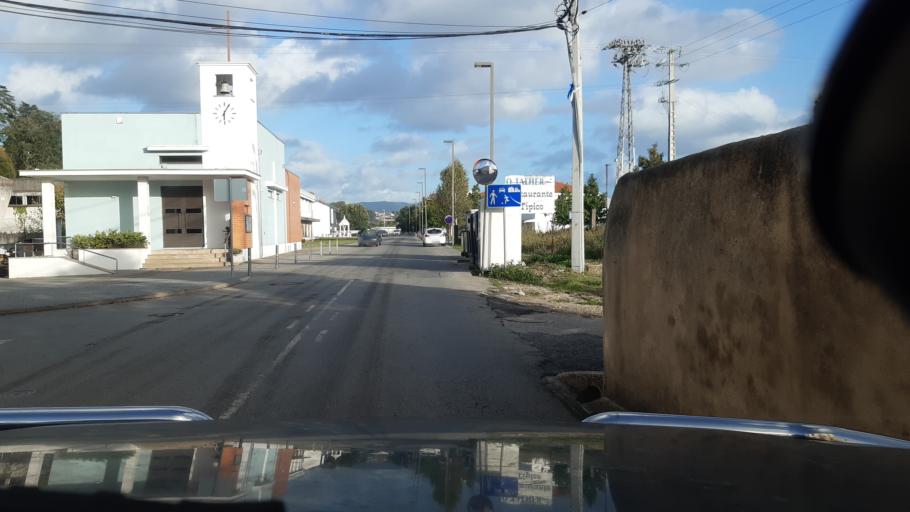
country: PT
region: Aveiro
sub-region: Agueda
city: Agueda
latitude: 40.5732
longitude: -8.4538
